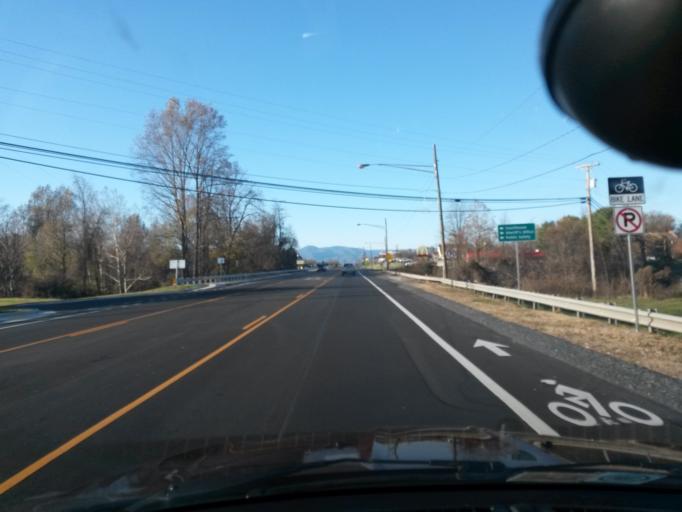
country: US
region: Virginia
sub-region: Amherst County
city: Amherst
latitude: 37.5854
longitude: -79.0480
